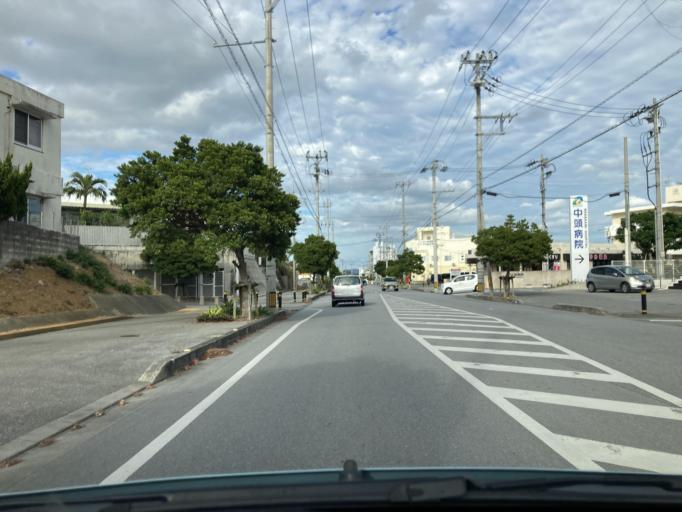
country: JP
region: Okinawa
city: Okinawa
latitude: 26.3667
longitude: 127.8244
